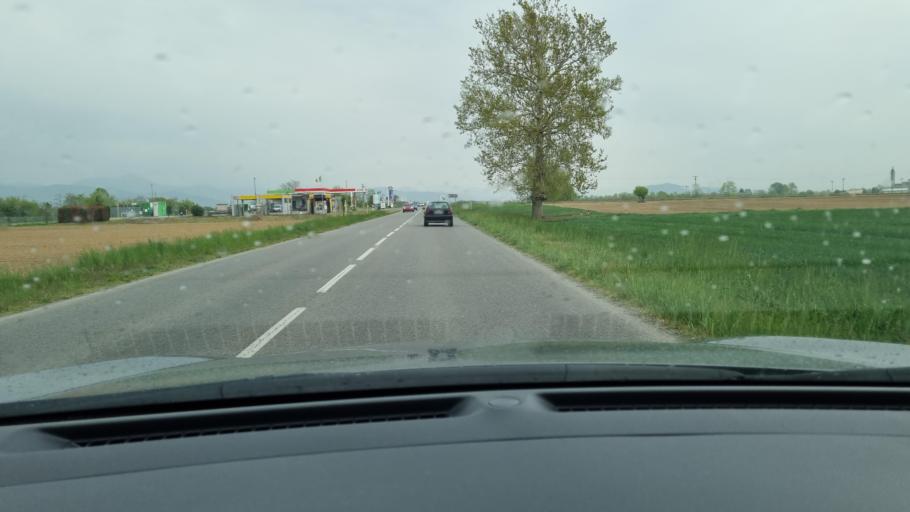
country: IT
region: Lombardy
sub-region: Provincia di Bergamo
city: Mornico al Serio
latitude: 45.5962
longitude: 9.7911
